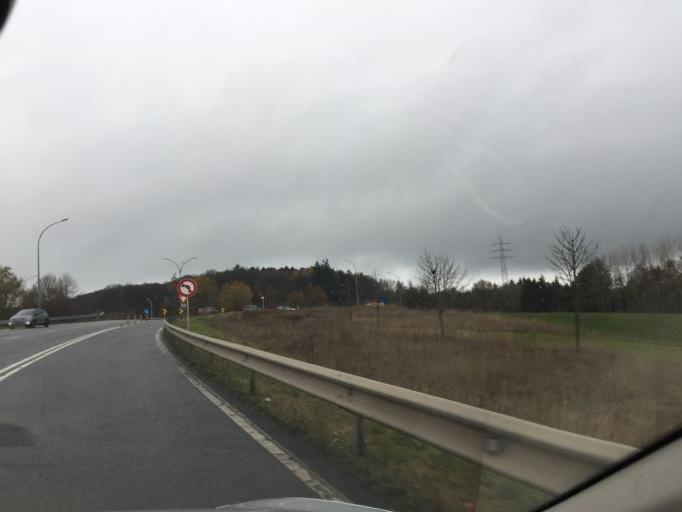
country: LU
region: Diekirch
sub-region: Canton de Diekirch
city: Diekirch
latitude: 49.8848
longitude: 6.1381
